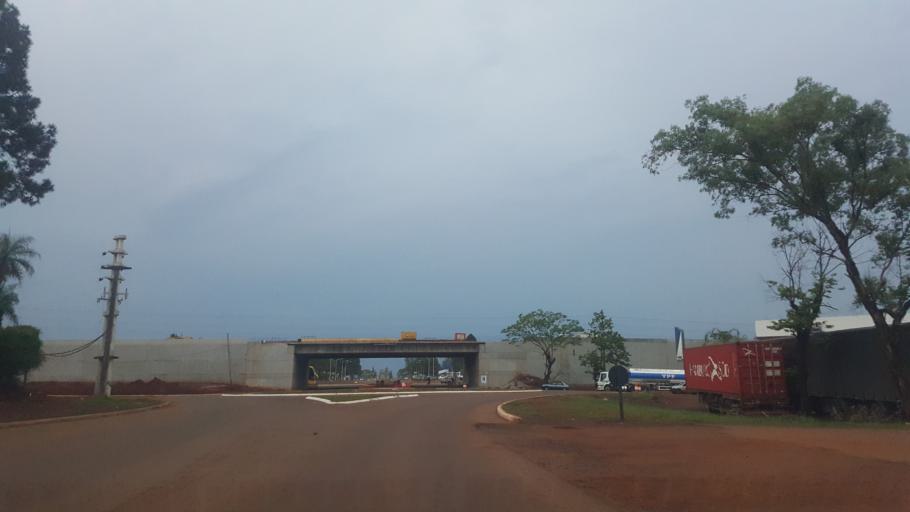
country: AR
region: Misiones
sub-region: Departamento de Candelaria
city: Candelaria
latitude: -27.4721
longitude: -55.7460
